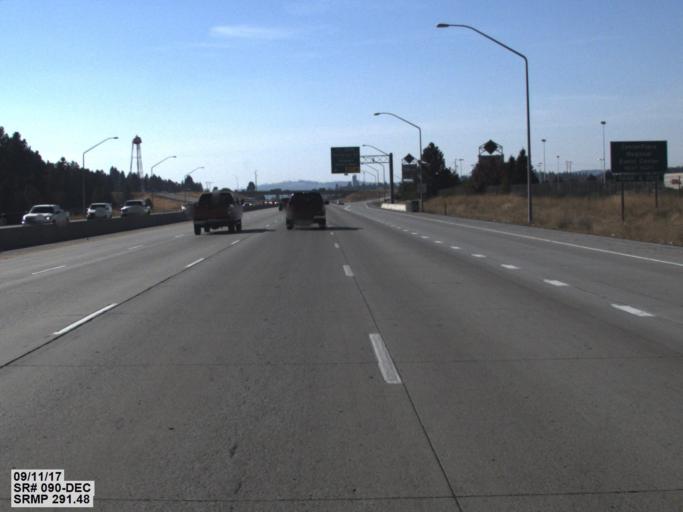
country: US
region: Washington
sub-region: Spokane County
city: Veradale
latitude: 47.6711
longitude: -117.2054
